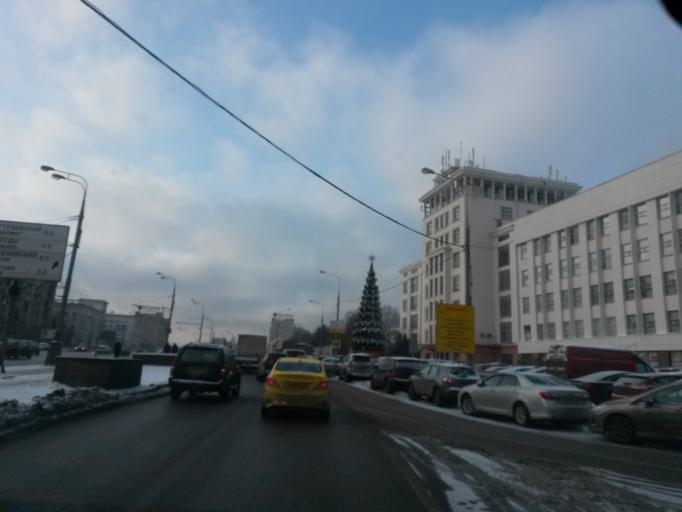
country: RU
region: Moskovskaya
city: Presnenskiy
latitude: 55.7396
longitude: 37.5314
